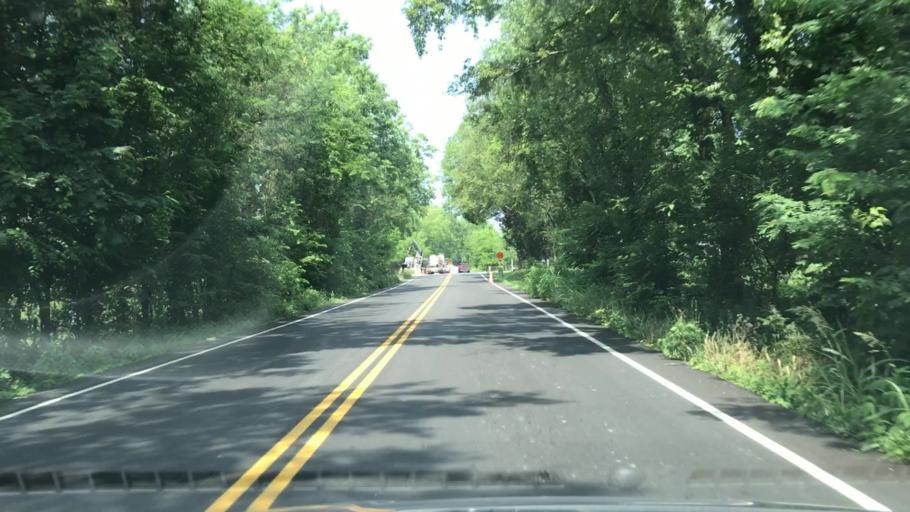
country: US
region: Tennessee
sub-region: Wilson County
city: Rural Hill
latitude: 36.1140
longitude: -86.4347
